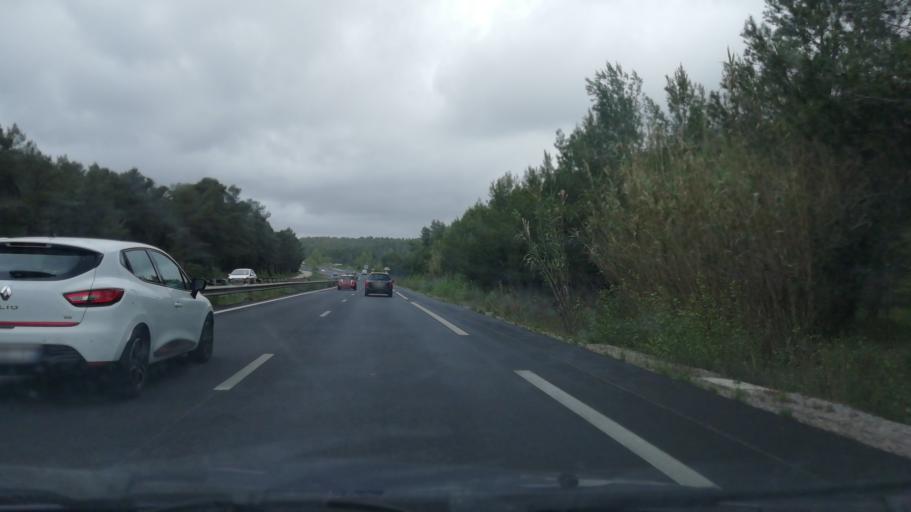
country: FR
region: Languedoc-Roussillon
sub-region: Departement de l'Herault
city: Saint-Clement-de-Riviere
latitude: 43.6665
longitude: 3.8278
